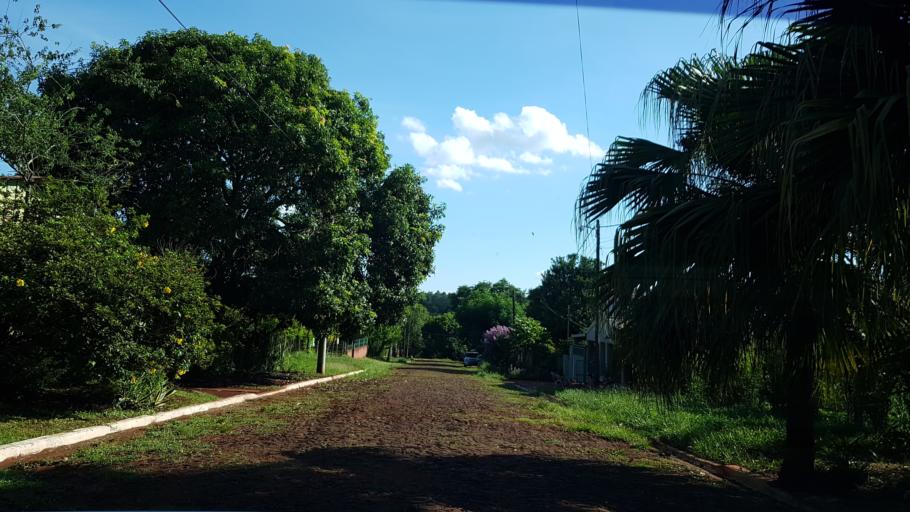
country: AR
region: Misiones
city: Puerto Libertad
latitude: -25.9192
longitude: -54.5778
